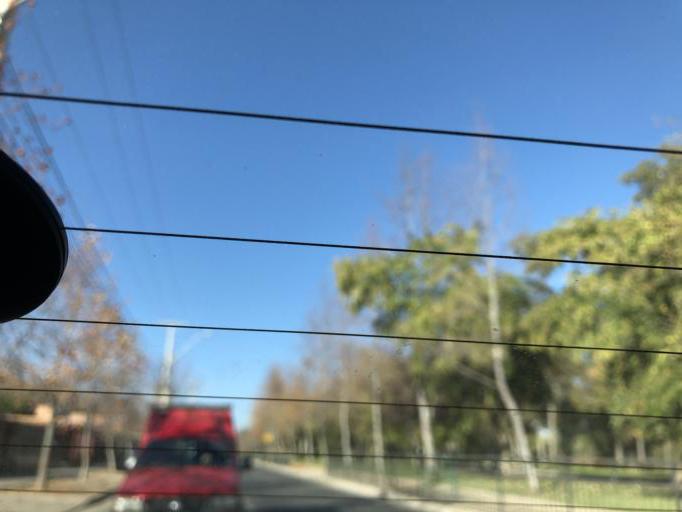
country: CL
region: Santiago Metropolitan
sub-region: Provincia de Cordillera
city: Puente Alto
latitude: -33.5537
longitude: -70.5531
